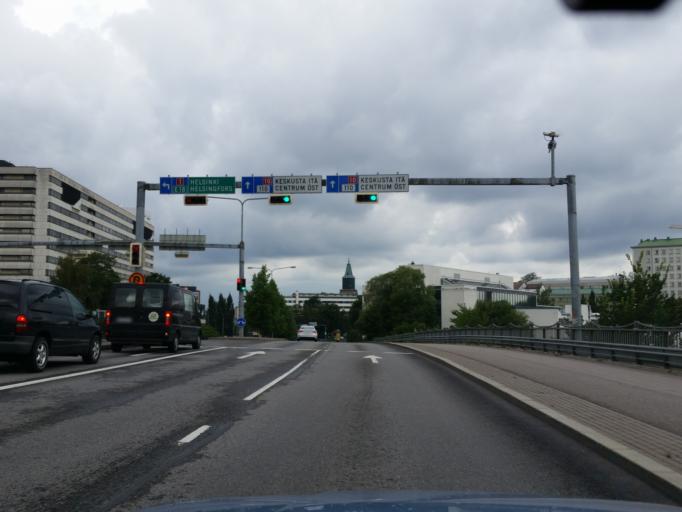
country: FI
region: Varsinais-Suomi
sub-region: Turku
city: Turku
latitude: 60.4547
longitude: 22.2928
